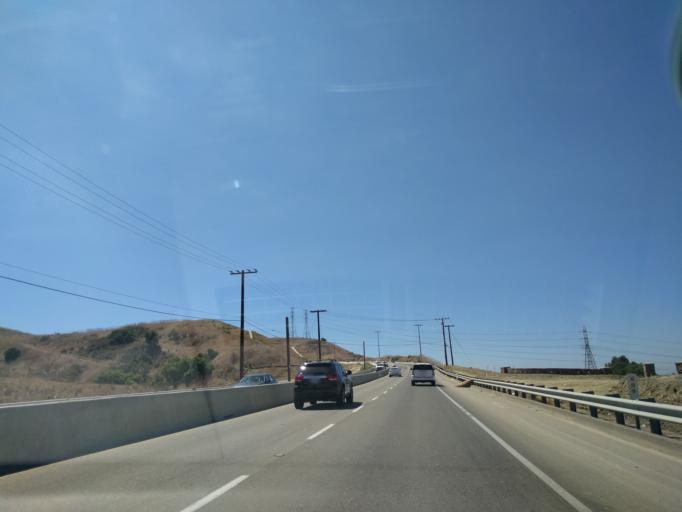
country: US
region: California
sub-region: Orange County
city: San Juan Capistrano
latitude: 33.5161
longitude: -117.6210
